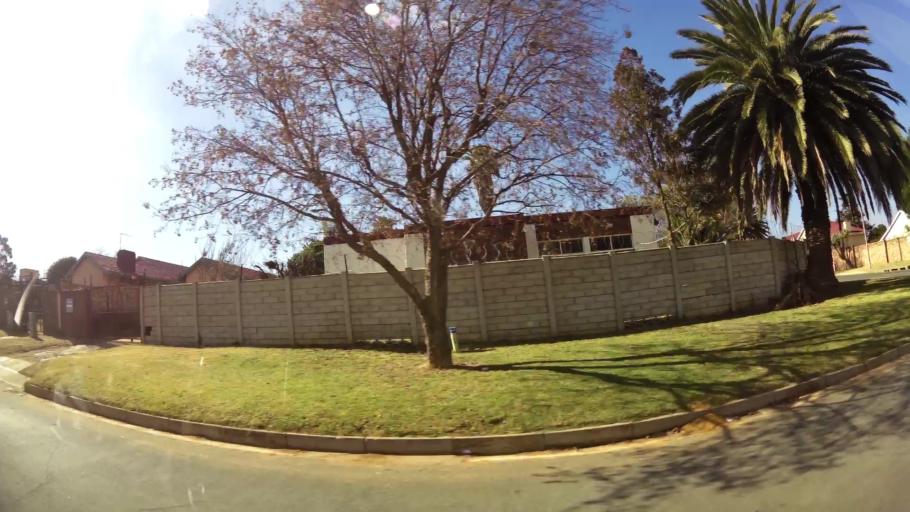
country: ZA
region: Gauteng
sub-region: City of Johannesburg Metropolitan Municipality
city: Roodepoort
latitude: -26.1424
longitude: 27.8223
